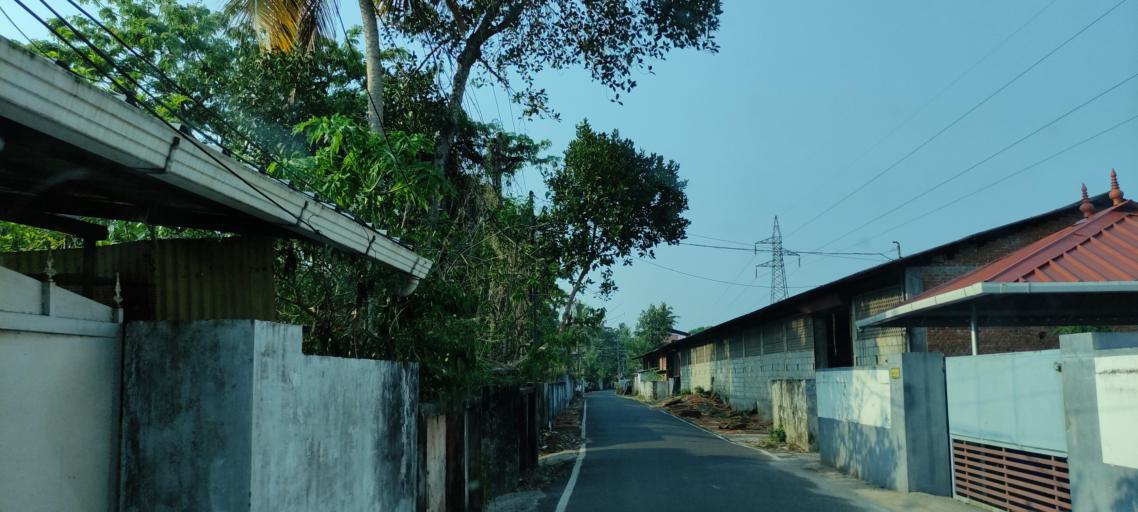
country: IN
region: Kerala
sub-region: Alappuzha
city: Alleppey
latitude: 9.5148
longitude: 76.3224
